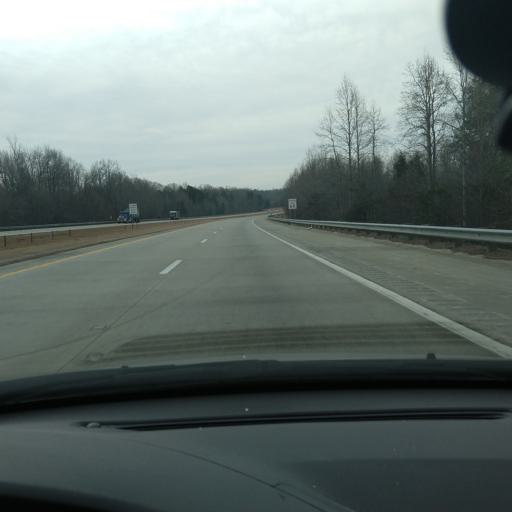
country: US
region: North Carolina
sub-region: Davidson County
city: Midway
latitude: 35.9326
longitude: -80.2323
